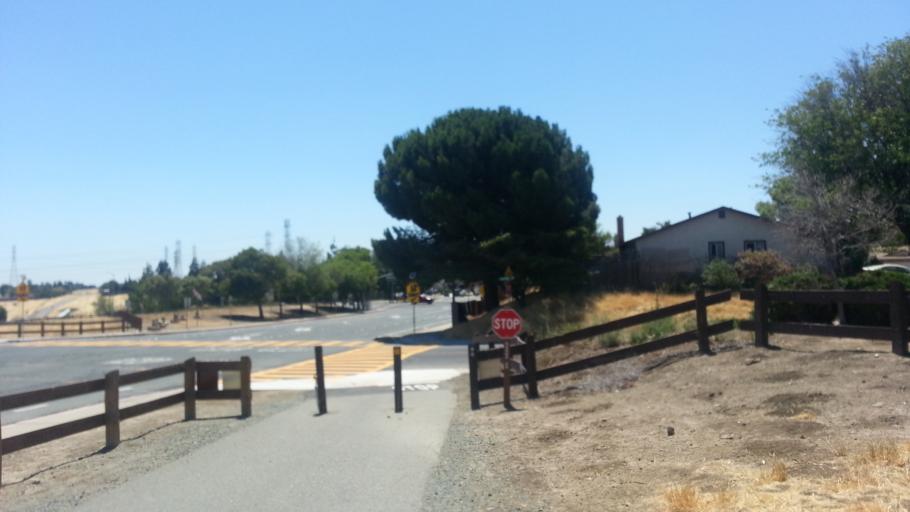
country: US
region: California
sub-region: Contra Costa County
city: Pittsburg
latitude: 38.0151
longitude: -121.9132
